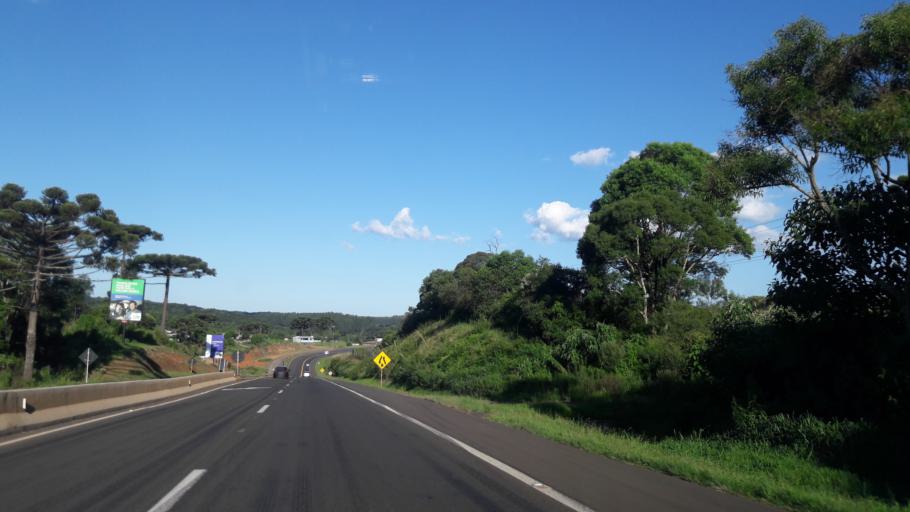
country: BR
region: Parana
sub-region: Guarapuava
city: Guarapuava
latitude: -25.3533
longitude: -51.3717
